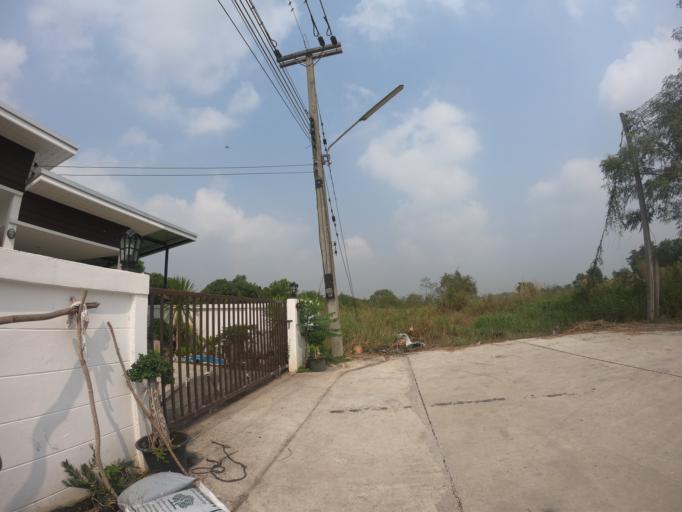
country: TH
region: Pathum Thani
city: Nong Suea
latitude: 14.0701
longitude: 100.8533
